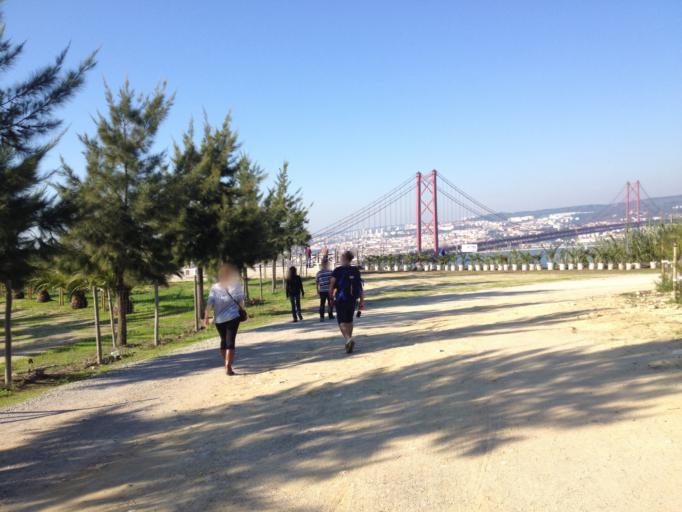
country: PT
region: Setubal
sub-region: Almada
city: Pragal
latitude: 38.6791
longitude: -9.1697
